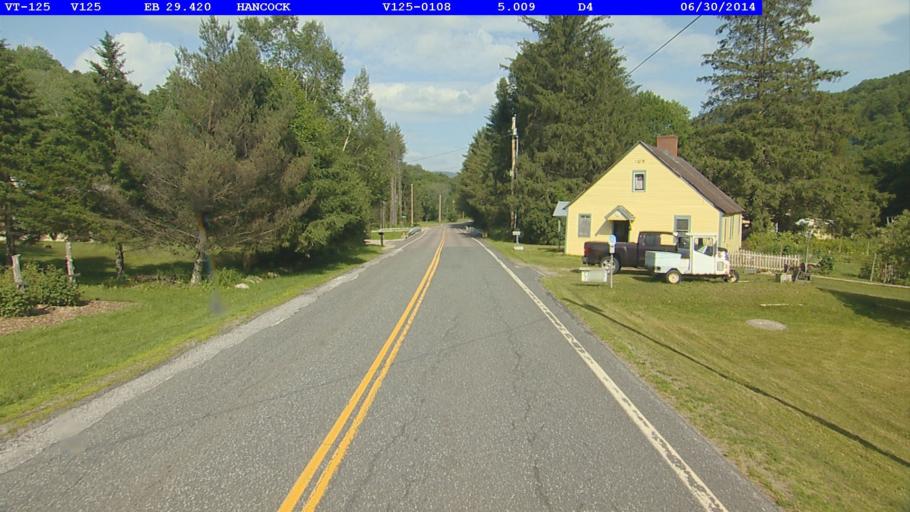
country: US
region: Vermont
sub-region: Orange County
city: Randolph
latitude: 43.9277
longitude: -72.8831
